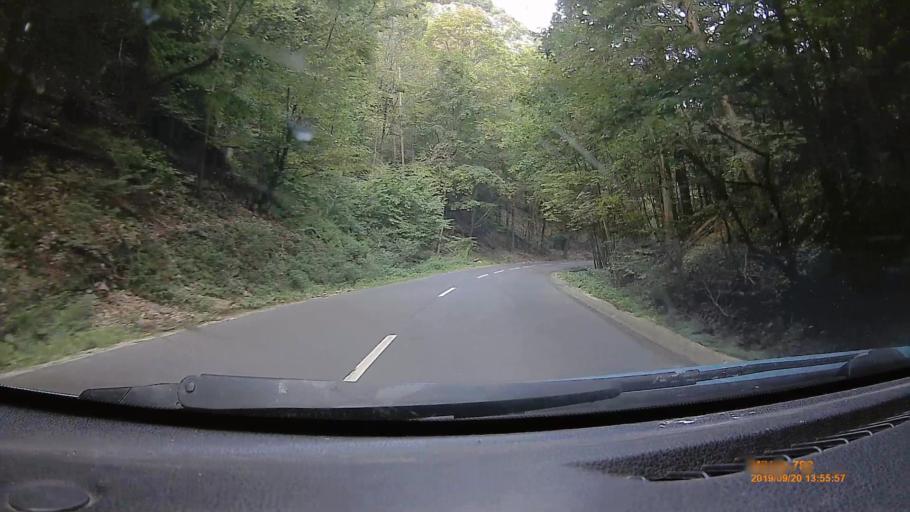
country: HU
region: Borsod-Abauj-Zemplen
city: Sajobabony
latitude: 48.0848
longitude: 20.6153
